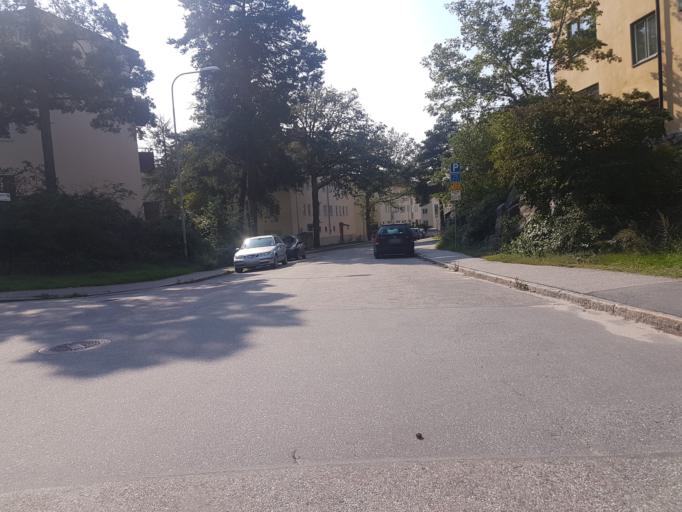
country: SE
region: Stockholm
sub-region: Stockholms Kommun
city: OEstermalm
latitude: 59.2967
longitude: 18.1130
